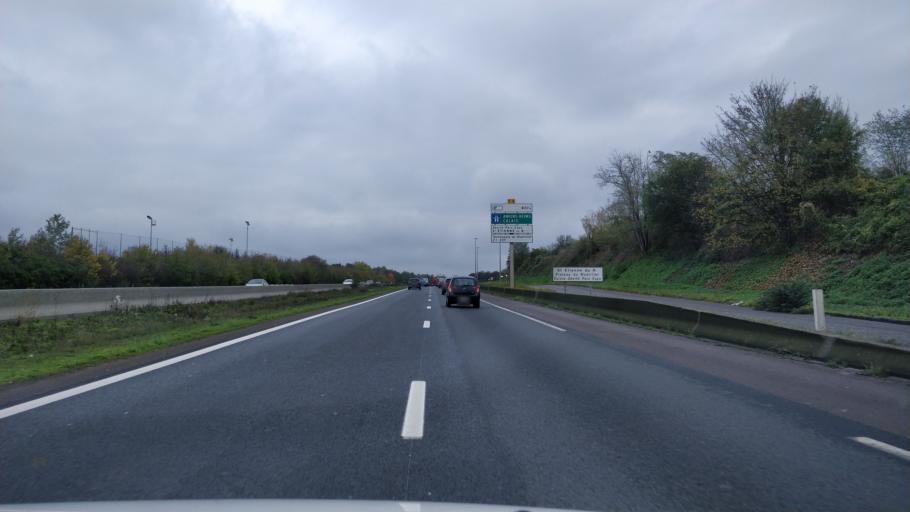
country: FR
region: Haute-Normandie
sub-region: Departement de la Seine-Maritime
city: Le Grand-Quevilly
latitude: 49.3929
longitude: 1.0382
